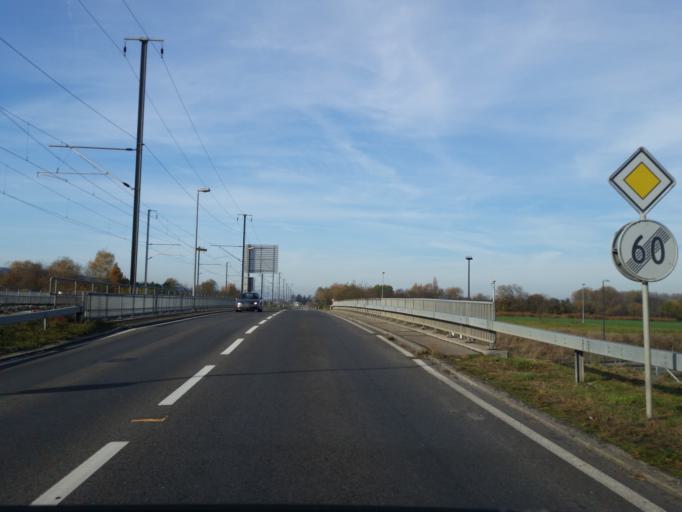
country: DE
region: Baden-Wuerttemberg
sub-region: Freiburg Region
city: Konstanz
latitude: 47.6550
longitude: 9.1595
